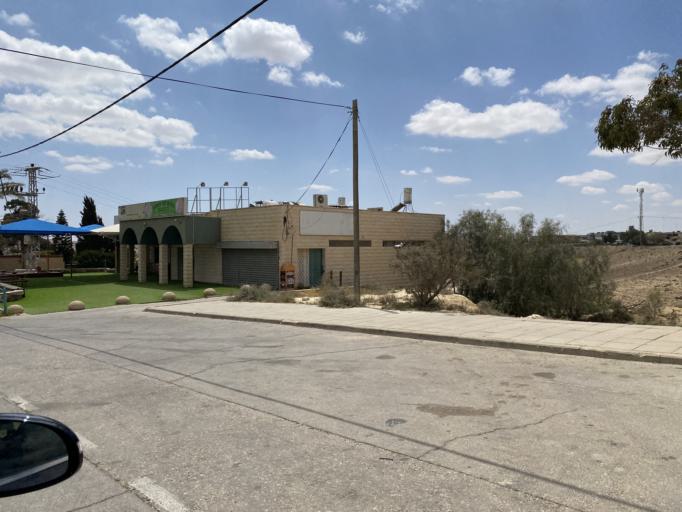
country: IL
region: Southern District
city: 'Arad
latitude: 31.2546
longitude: 35.2148
